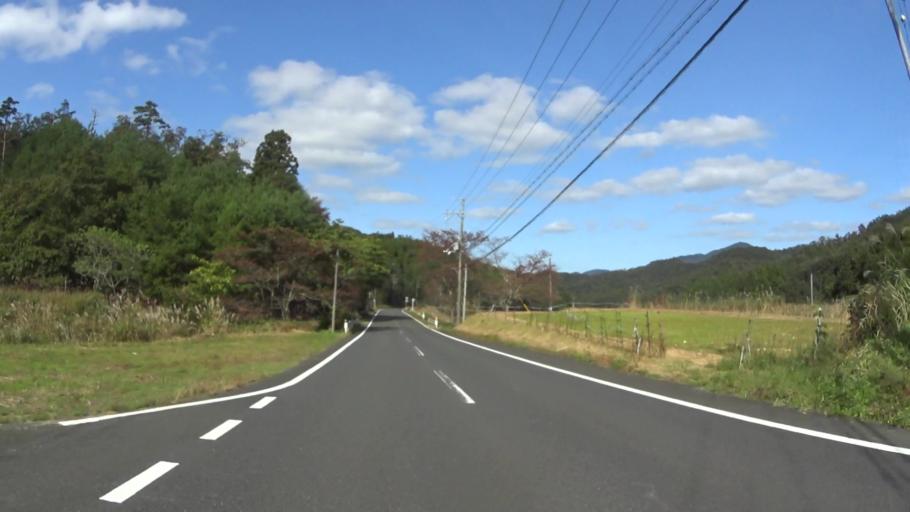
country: JP
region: Hyogo
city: Toyooka
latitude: 35.5510
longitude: 134.9773
